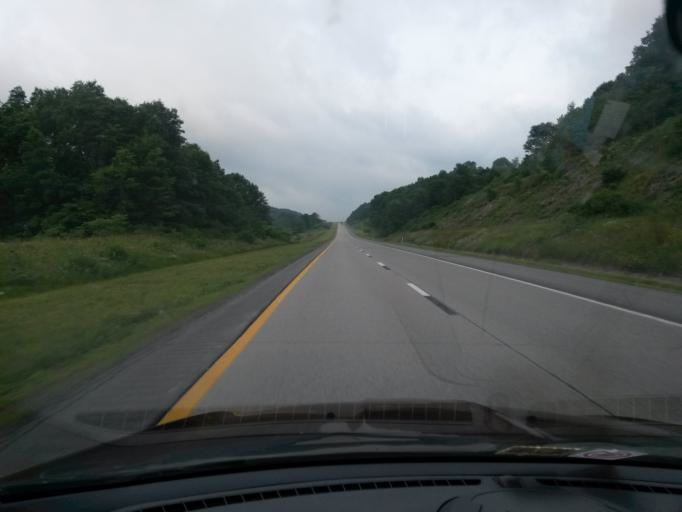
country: US
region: West Virginia
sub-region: Greenbrier County
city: Rainelle
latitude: 37.8433
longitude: -80.7359
